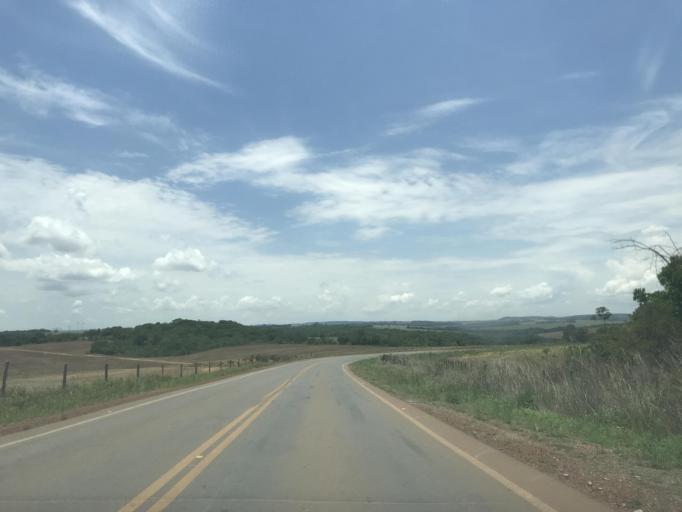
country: BR
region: Goias
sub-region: Vianopolis
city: Vianopolis
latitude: -16.6334
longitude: -48.3556
